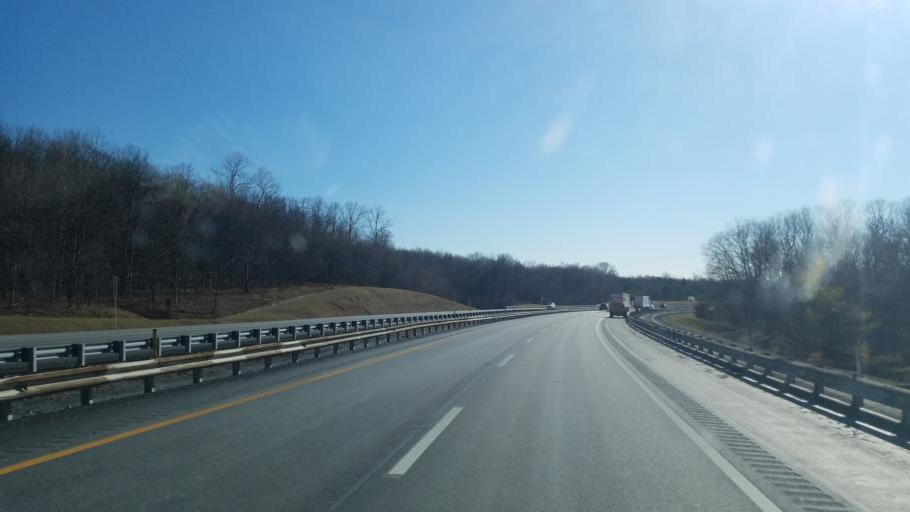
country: US
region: Pennsylvania
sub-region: Bedford County
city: Earlston
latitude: 39.9878
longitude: -78.2313
